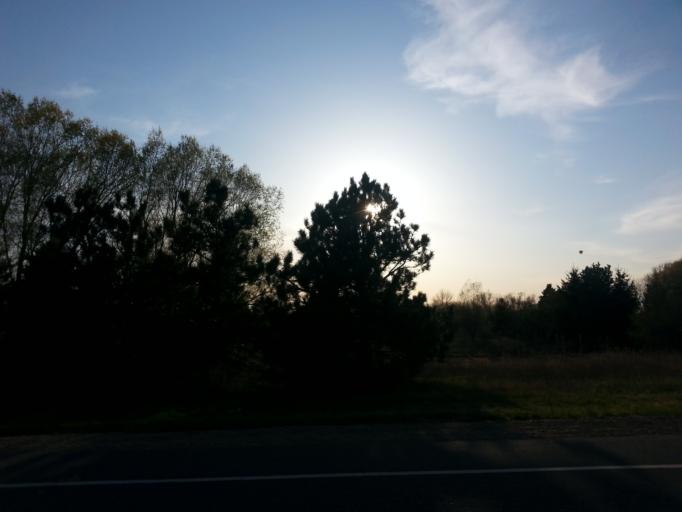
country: US
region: Minnesota
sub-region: Washington County
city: Lake Saint Croix Beach
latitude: 44.9306
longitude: -92.6978
